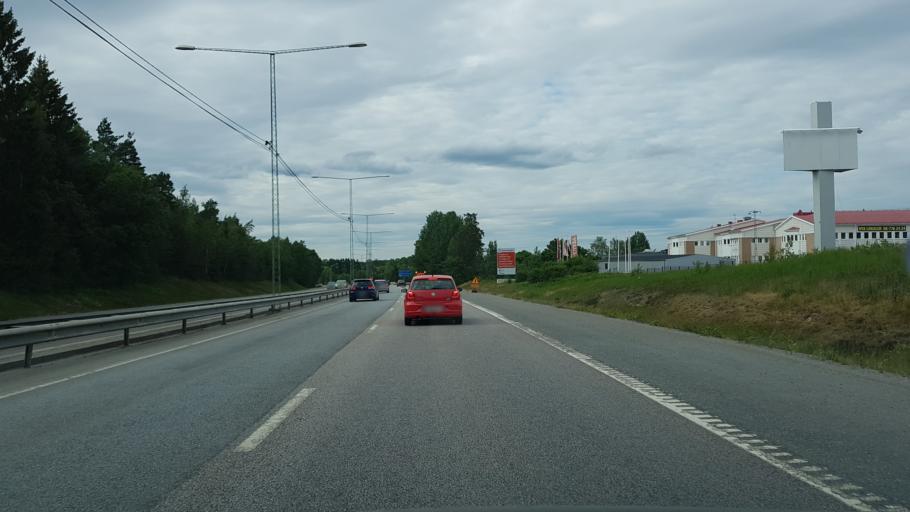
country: SE
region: Stockholm
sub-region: Haninge Kommun
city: Haninge
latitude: 59.1742
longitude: 18.1586
